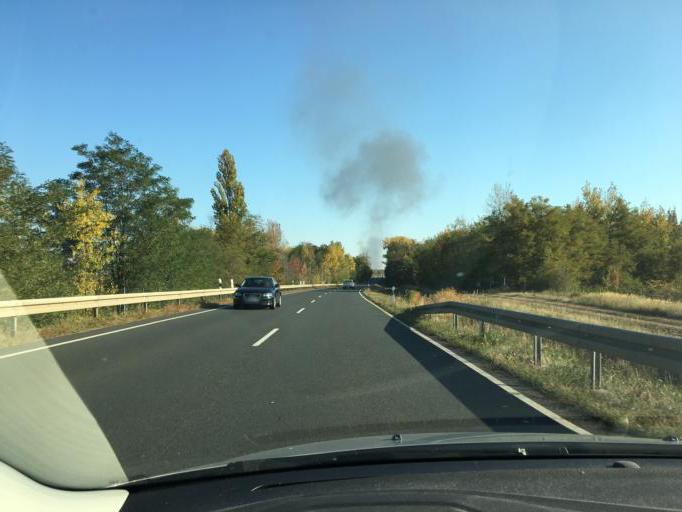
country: DE
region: Saxony-Anhalt
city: Sandersdorf
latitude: 51.6424
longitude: 12.2654
